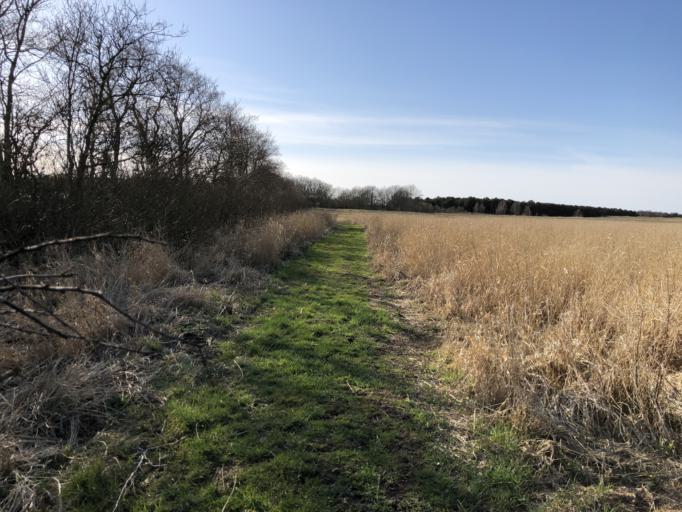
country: DK
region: Central Jutland
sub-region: Holstebro Kommune
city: Ulfborg
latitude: 56.3227
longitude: 8.3251
